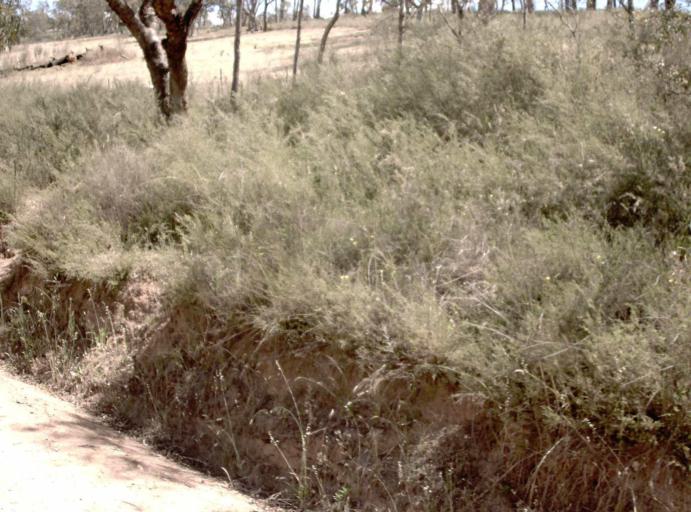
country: AU
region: New South Wales
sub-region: Snowy River
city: Jindabyne
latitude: -37.0566
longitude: 148.5712
